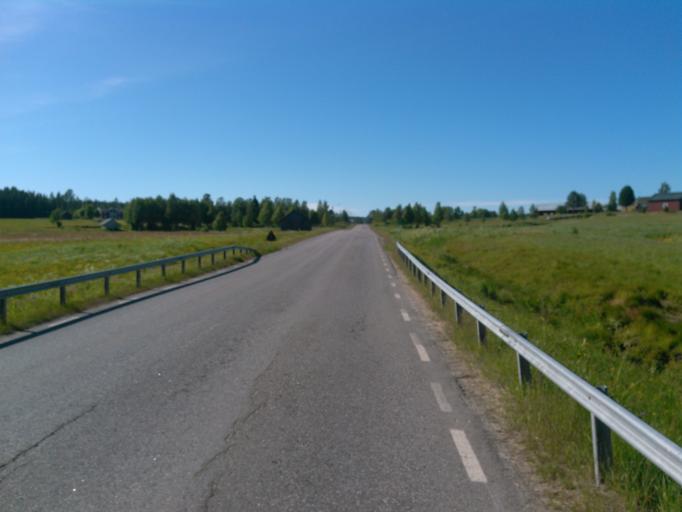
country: SE
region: Vaesterbotten
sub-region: Umea Kommun
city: Roback
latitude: 63.8239
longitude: 20.1255
